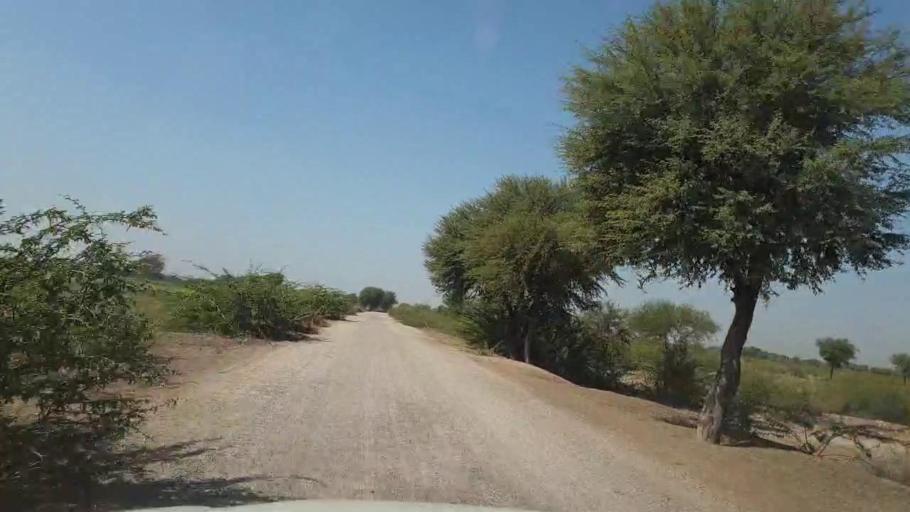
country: PK
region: Sindh
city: Kunri
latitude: 25.1253
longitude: 69.5357
